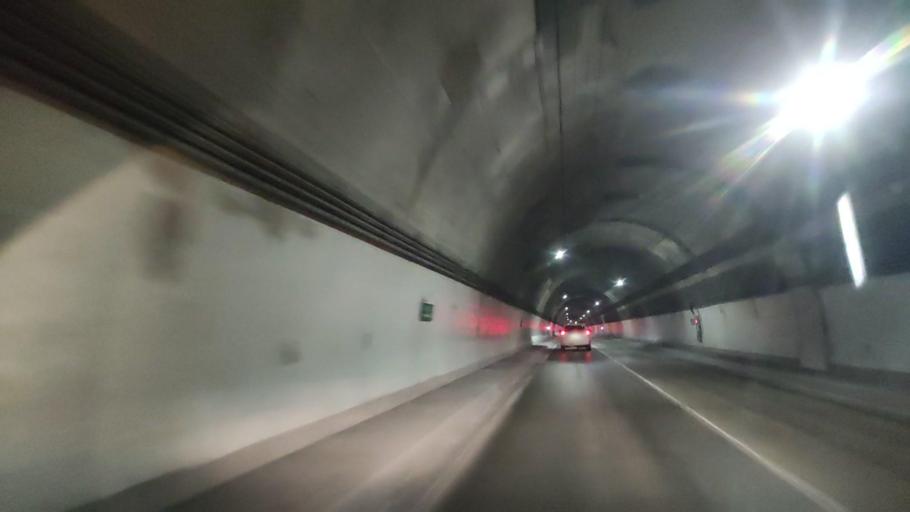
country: JP
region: Hokkaido
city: Ishikari
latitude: 43.4464
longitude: 141.4118
